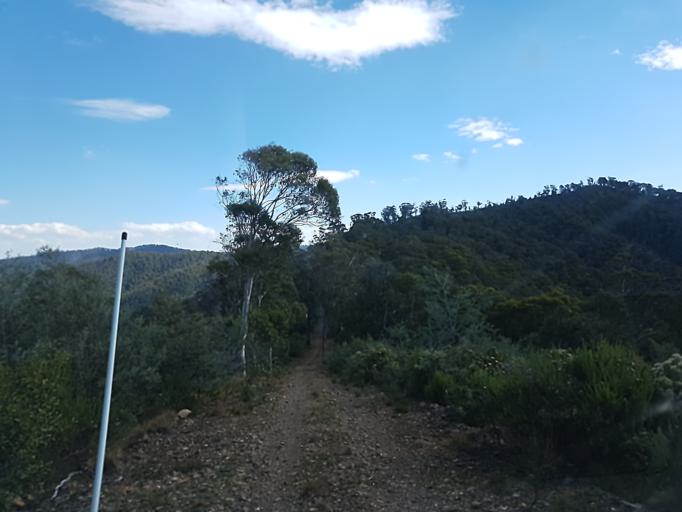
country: AU
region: Victoria
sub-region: Alpine
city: Mount Beauty
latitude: -36.9096
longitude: 147.0175
